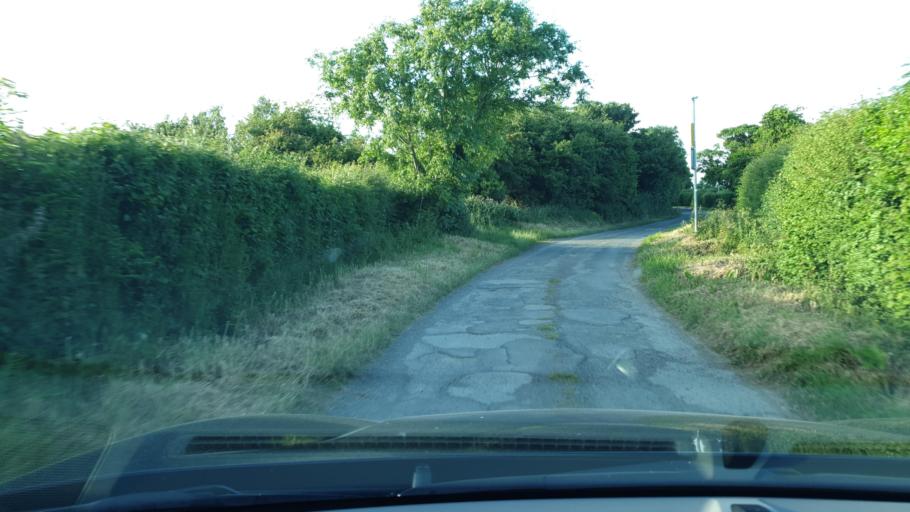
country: IE
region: Leinster
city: Hartstown
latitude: 53.4358
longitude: -6.4036
